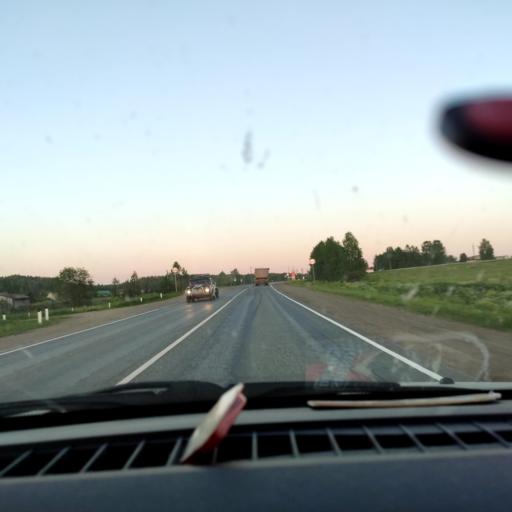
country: RU
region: Perm
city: Mendeleyevo
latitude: 58.1076
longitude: 55.1159
